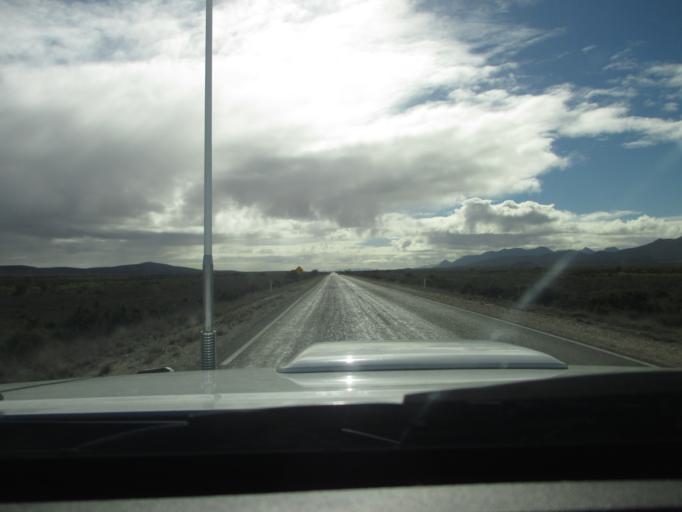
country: AU
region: South Australia
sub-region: Flinders Ranges
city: Quorn
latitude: -31.6735
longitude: 138.3693
